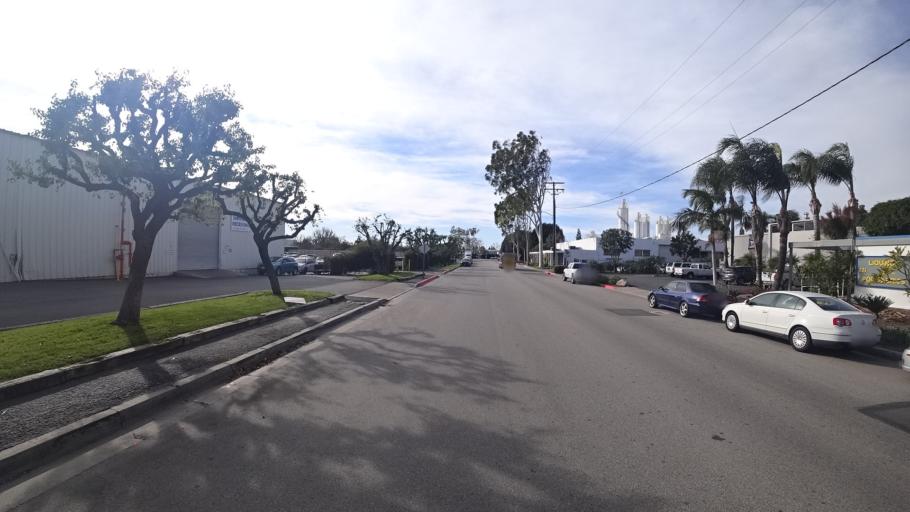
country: US
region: California
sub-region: Orange County
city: Orange
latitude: 33.8229
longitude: -117.8543
